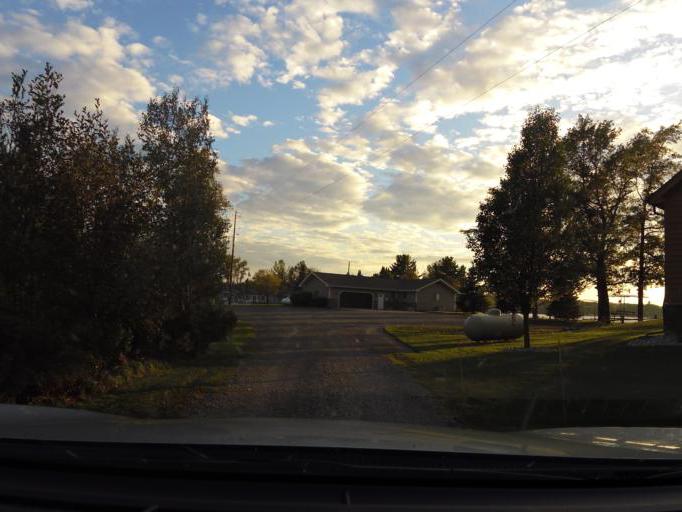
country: US
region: Michigan
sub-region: Roscommon County
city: Saint Helen
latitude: 44.3593
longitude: -84.4731
